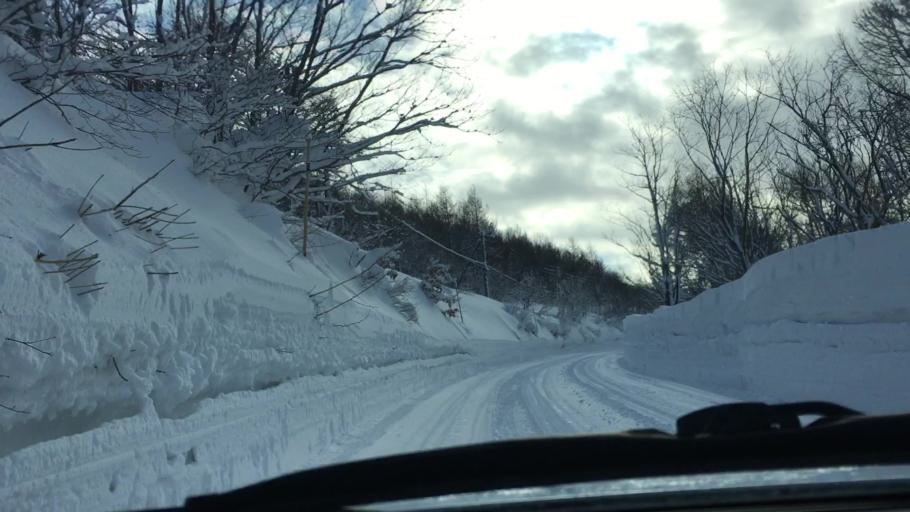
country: JP
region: Aomori
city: Aomori Shi
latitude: 40.6484
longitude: 140.7815
